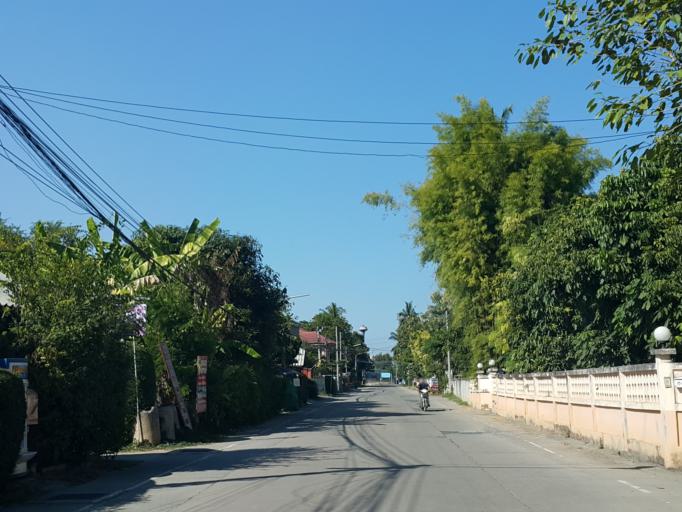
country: TH
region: Chiang Mai
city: San Sai
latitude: 18.8832
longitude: 99.0122
